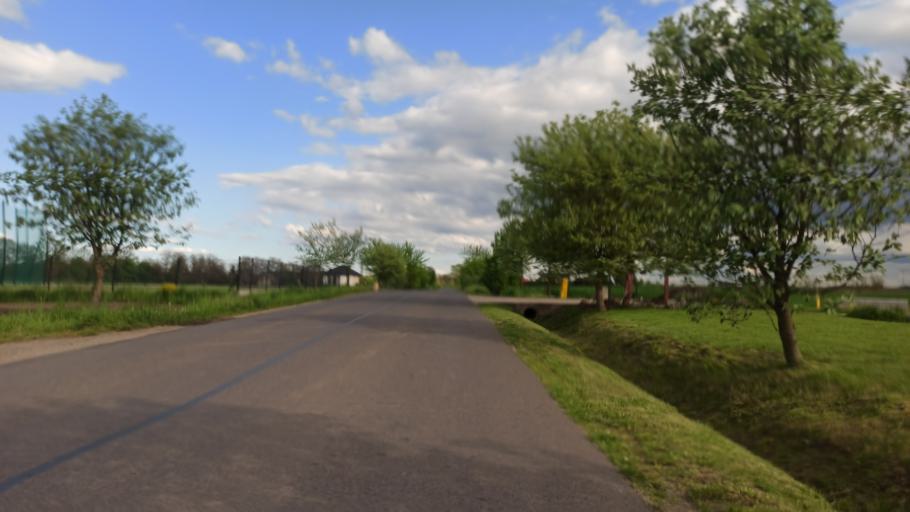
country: PL
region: Subcarpathian Voivodeship
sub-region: Powiat jaroslawski
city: Sosnica
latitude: 49.9226
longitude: 22.8526
